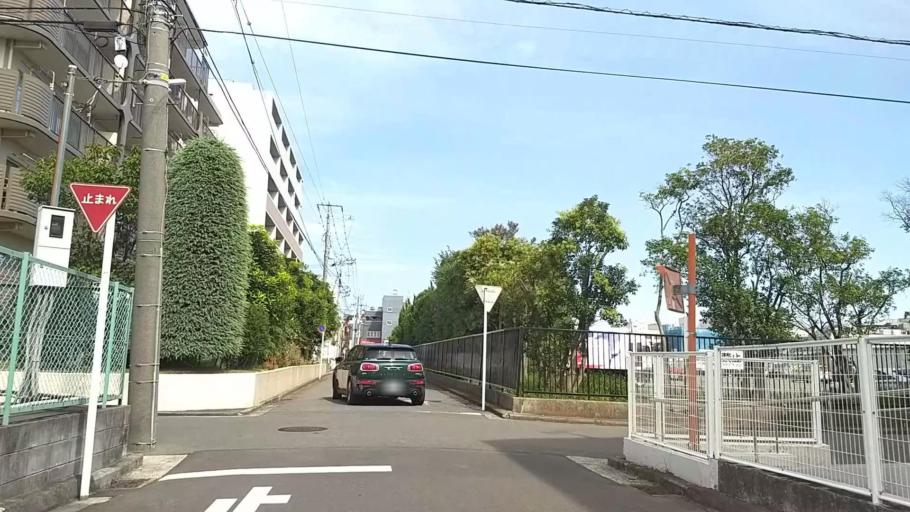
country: JP
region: Kanagawa
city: Yokohama
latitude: 35.5204
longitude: 139.5727
